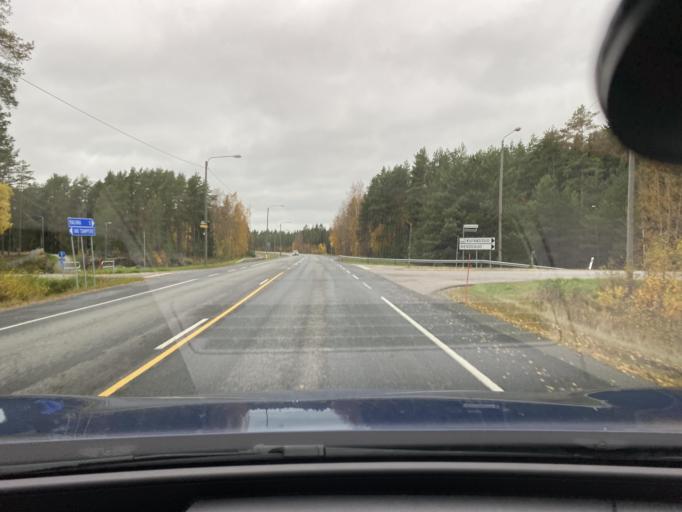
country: FI
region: Satakunta
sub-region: Rauma
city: Rauma
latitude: 61.1341
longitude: 21.5934
